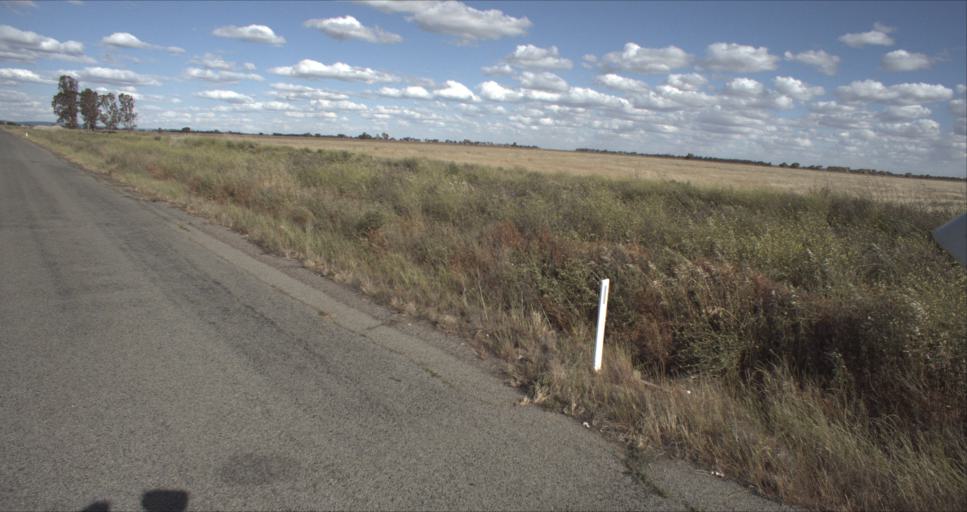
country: AU
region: New South Wales
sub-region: Leeton
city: Leeton
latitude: -34.4416
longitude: 146.2349
